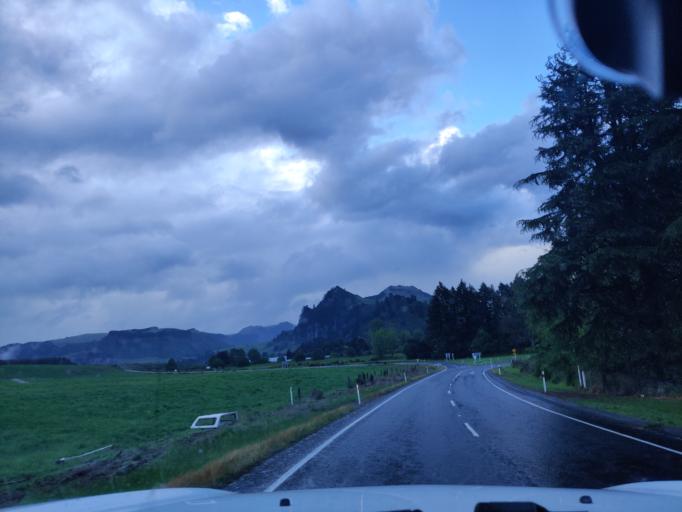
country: NZ
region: Waikato
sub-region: South Waikato District
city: Tokoroa
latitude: -38.4171
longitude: 175.8111
